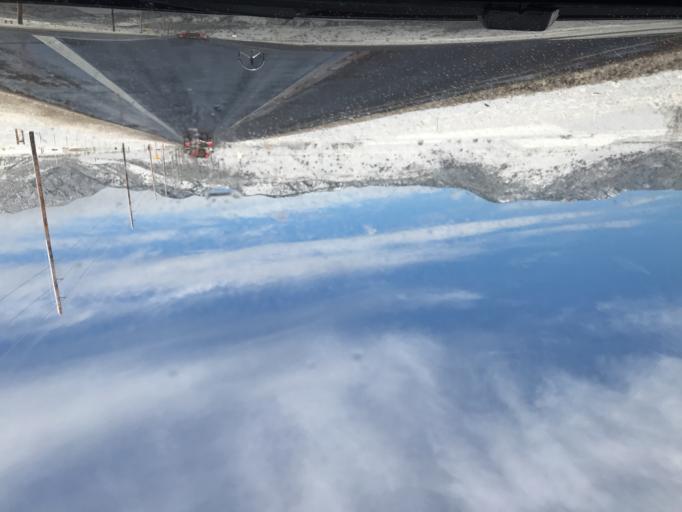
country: US
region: Colorado
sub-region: Boulder County
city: Superior
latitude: 39.8651
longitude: -105.2313
